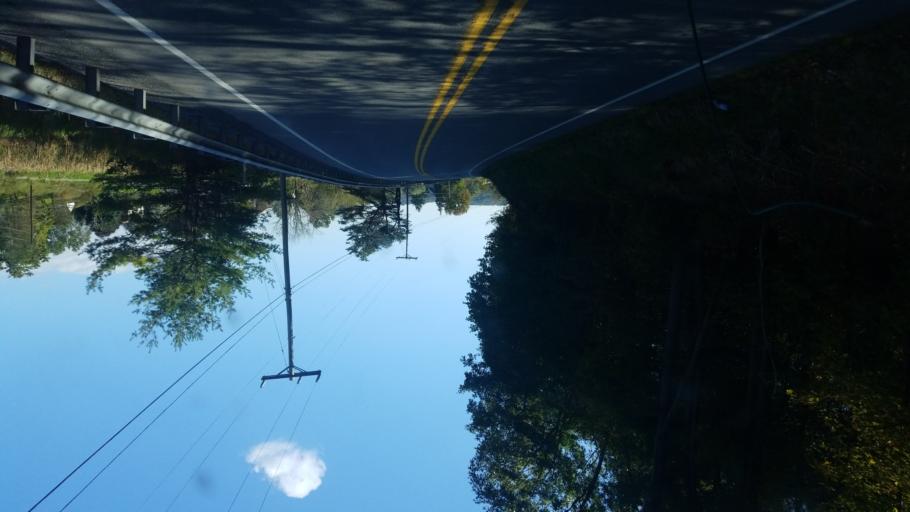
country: US
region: Pennsylvania
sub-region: Blair County
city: Claysburg
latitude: 40.1740
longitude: -78.5162
